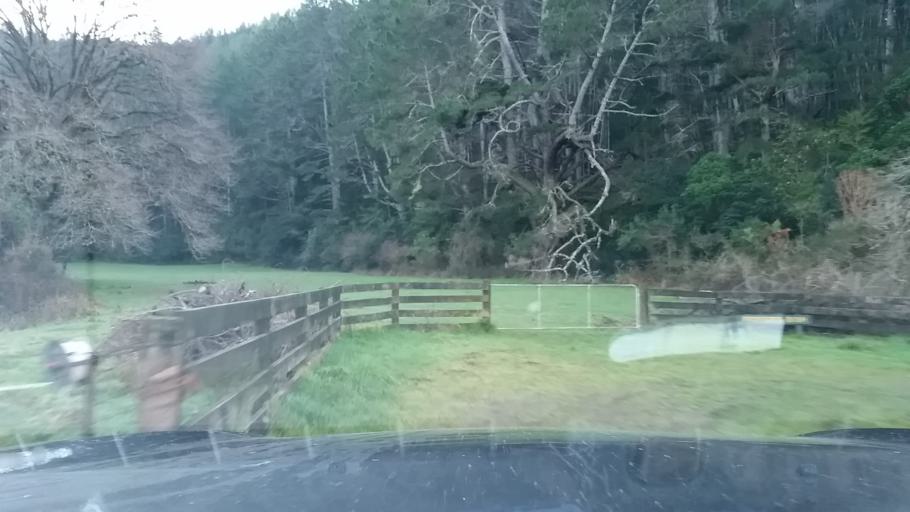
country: NZ
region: Marlborough
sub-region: Marlborough District
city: Blenheim
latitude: -41.4686
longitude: 173.7438
